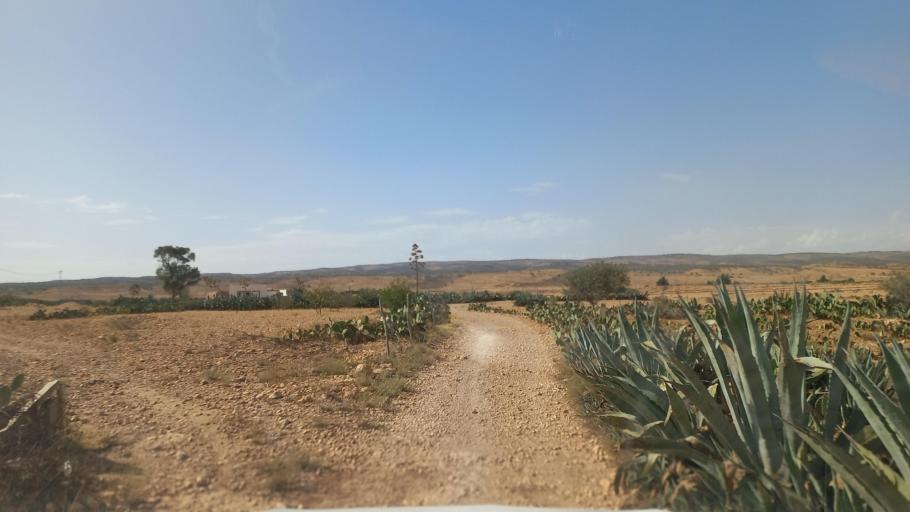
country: TN
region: Al Qasrayn
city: Kasserine
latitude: 35.2867
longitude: 8.9380
